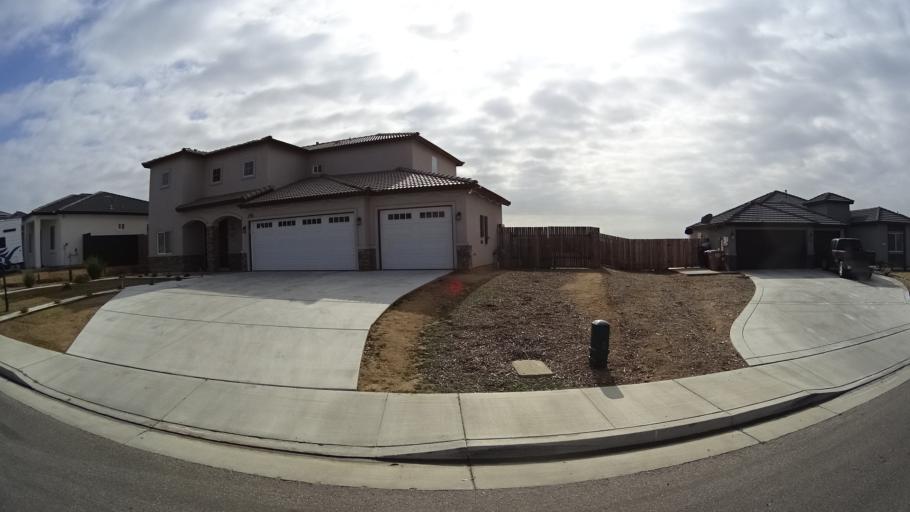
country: US
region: California
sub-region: Kern County
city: Bakersfield
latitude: 35.3875
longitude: -118.9267
